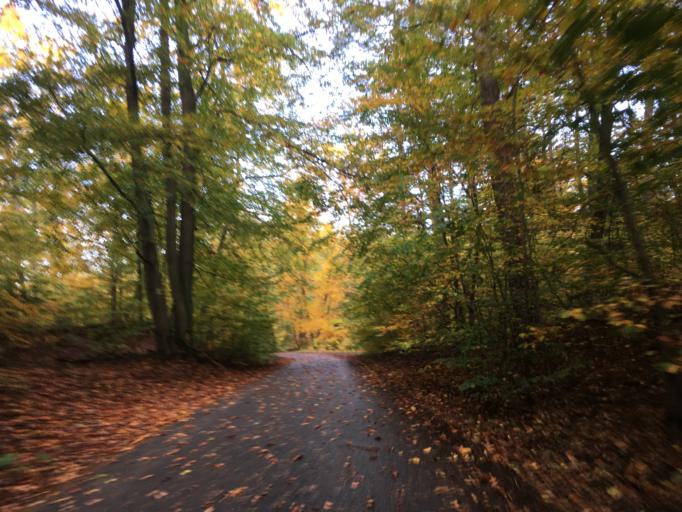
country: DE
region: Brandenburg
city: Wandlitz
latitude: 52.7292
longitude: 13.4614
